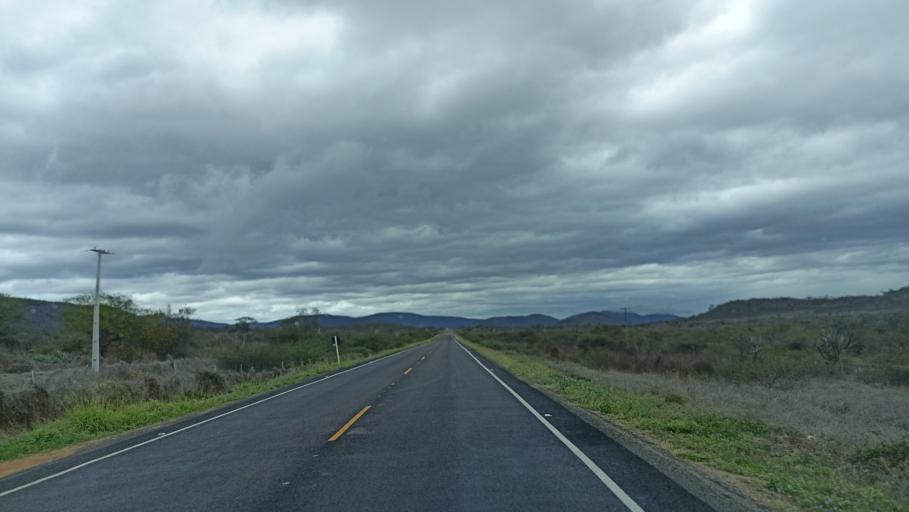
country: BR
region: Bahia
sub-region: Iacu
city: Iacu
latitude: -12.9025
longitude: -40.4035
